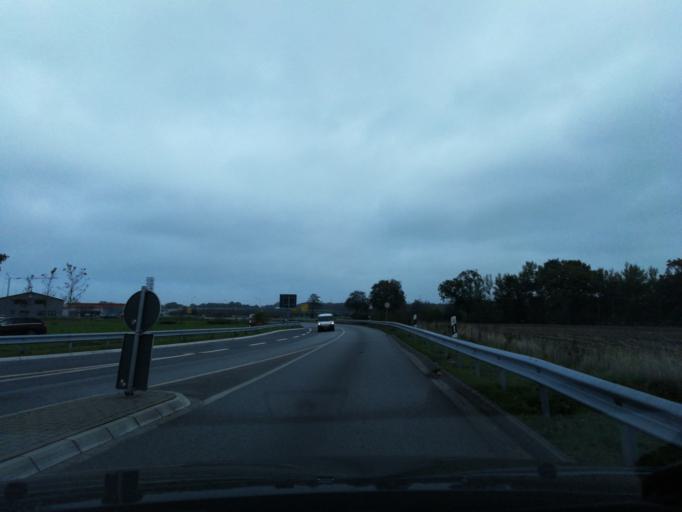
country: DE
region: Lower Saxony
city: Schortens
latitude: 53.5373
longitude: 7.9687
